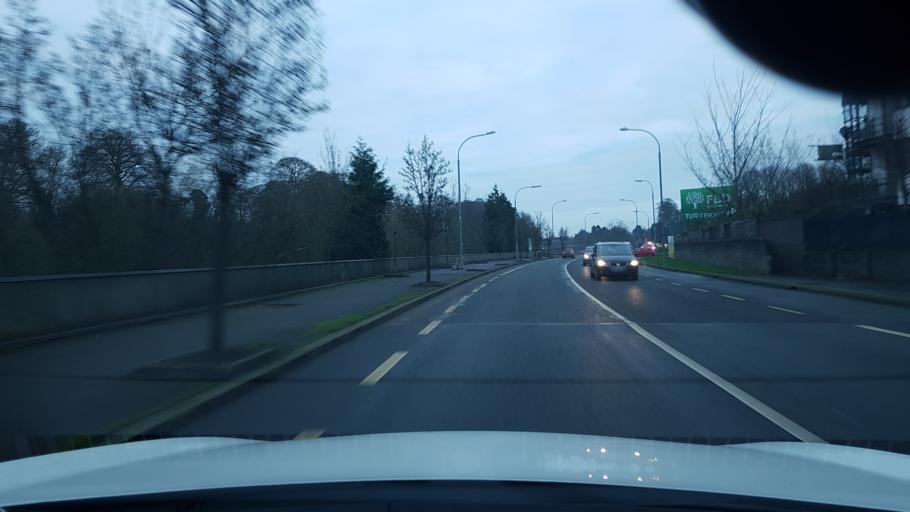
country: IE
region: Leinster
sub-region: An Mhi
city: Navan
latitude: 53.6469
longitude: -6.6748
